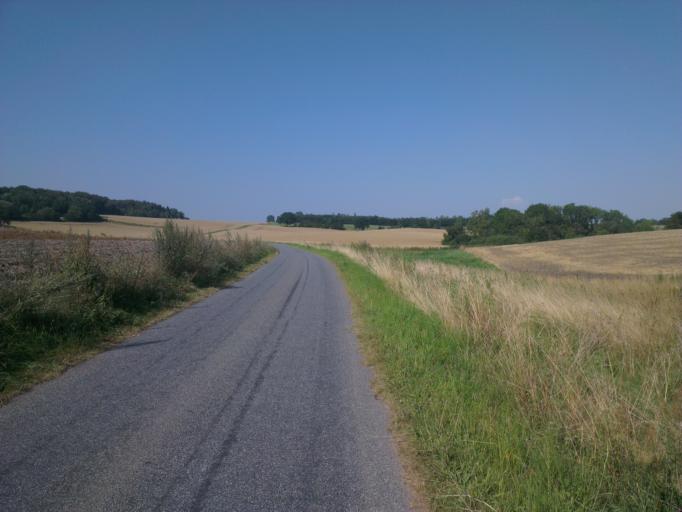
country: DK
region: Capital Region
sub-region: Frederikssund Kommune
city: Skibby
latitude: 55.7576
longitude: 11.9436
